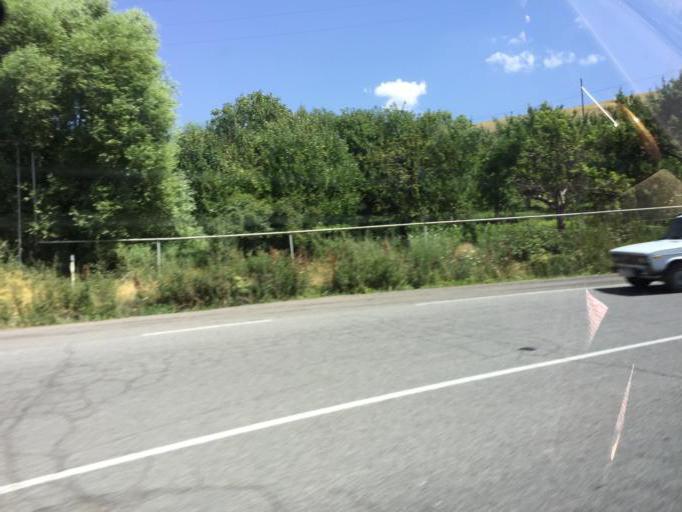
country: AM
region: Vayots' Dzori Marz
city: Jermuk
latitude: 39.7221
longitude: 45.6456
